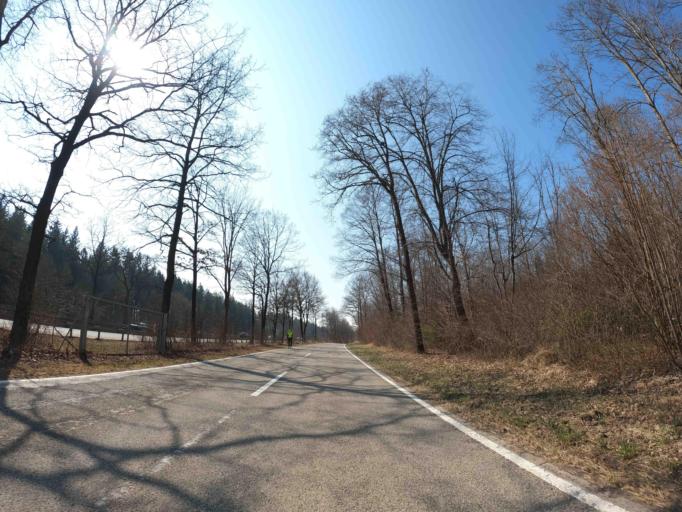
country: DE
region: Bavaria
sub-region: Upper Bavaria
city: Baierbrunn
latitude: 48.0456
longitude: 11.4456
